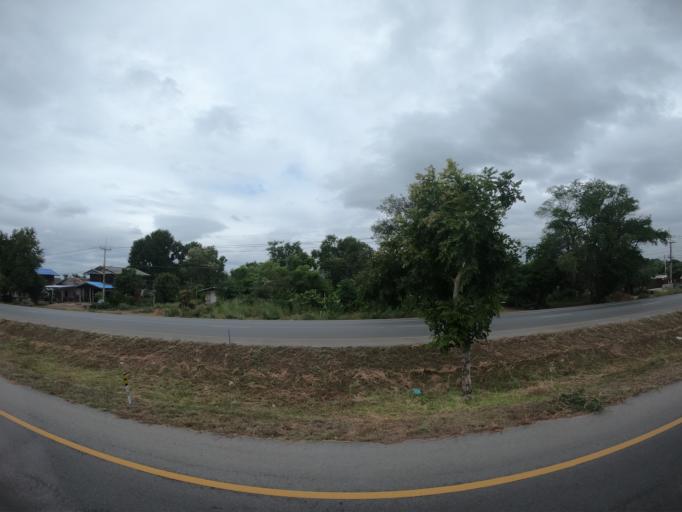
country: TH
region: Khon Kaen
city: Ban Phai
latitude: 16.0443
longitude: 102.8393
